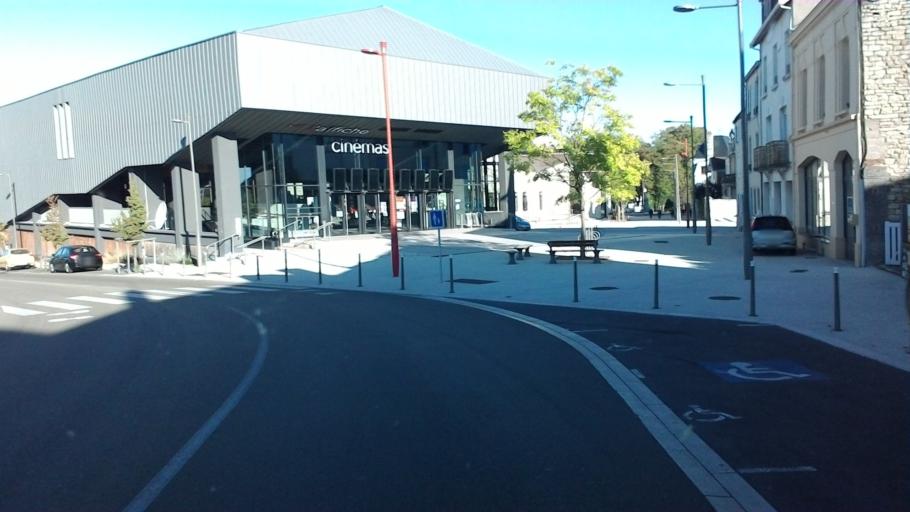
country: FR
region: Champagne-Ardenne
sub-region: Departement de la Haute-Marne
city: Chaumont
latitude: 48.1098
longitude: 5.1362
